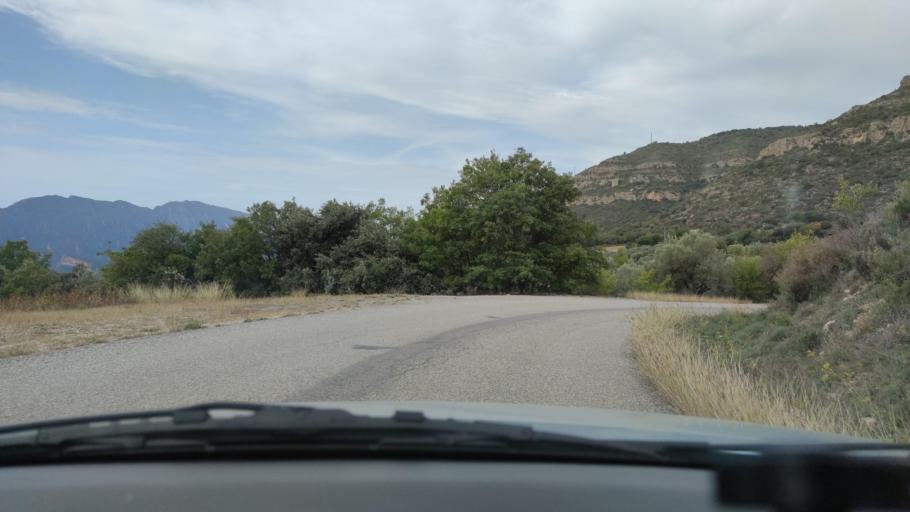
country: ES
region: Catalonia
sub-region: Provincia de Lleida
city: Llimiana
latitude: 42.0680
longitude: 0.9502
